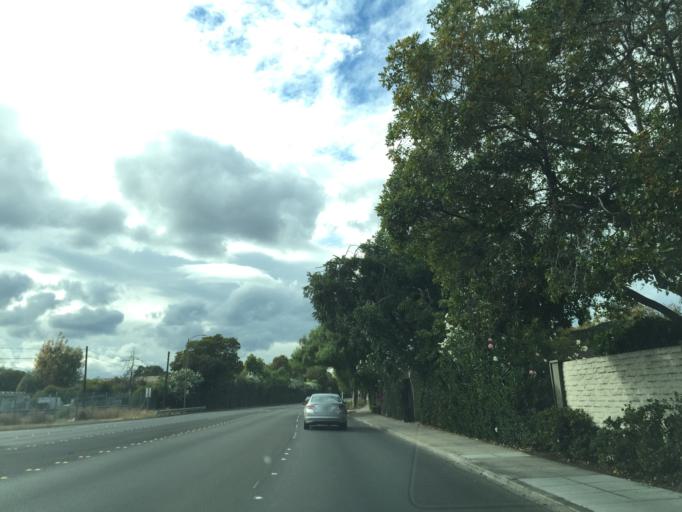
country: US
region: California
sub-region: Santa Clara County
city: Los Altos
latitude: 37.4092
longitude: -122.1093
